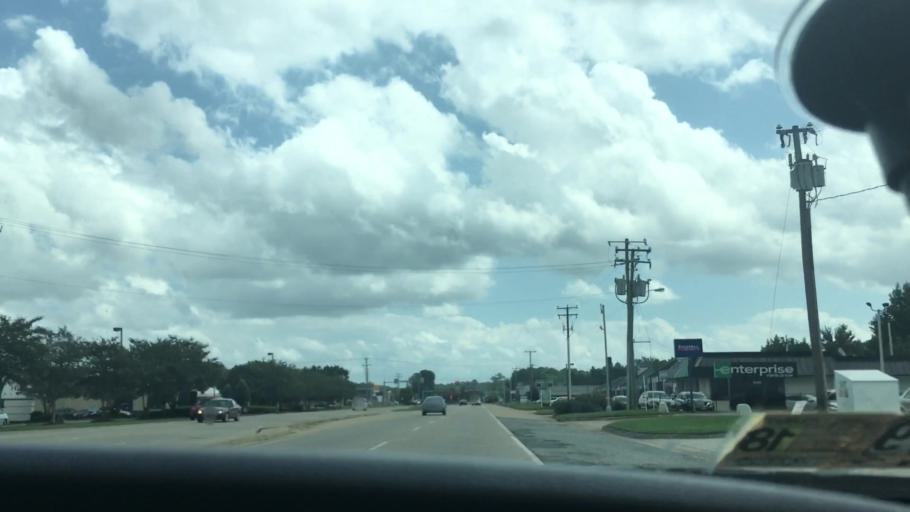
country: US
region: Virginia
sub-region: City of Portsmouth
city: Portsmouth Heights
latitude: 36.8631
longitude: -76.4041
